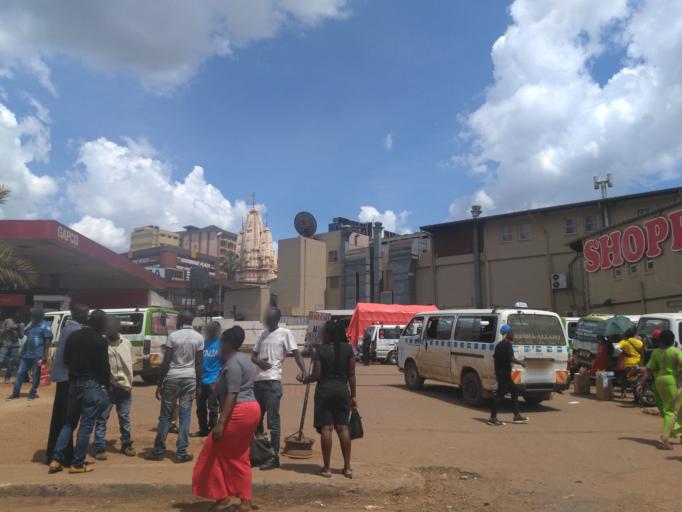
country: UG
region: Central Region
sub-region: Kampala District
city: Kampala
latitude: 0.3098
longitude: 32.5774
